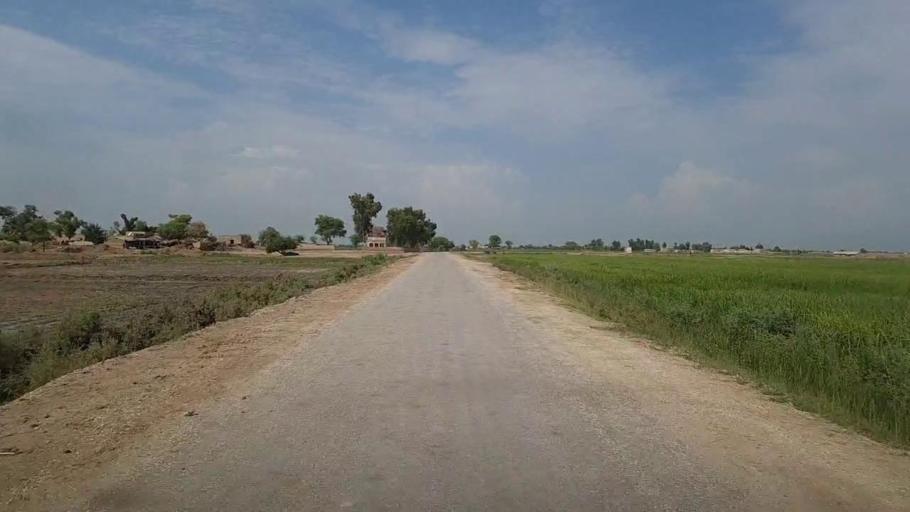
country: PK
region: Sindh
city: Thul
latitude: 28.2907
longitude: 68.8221
